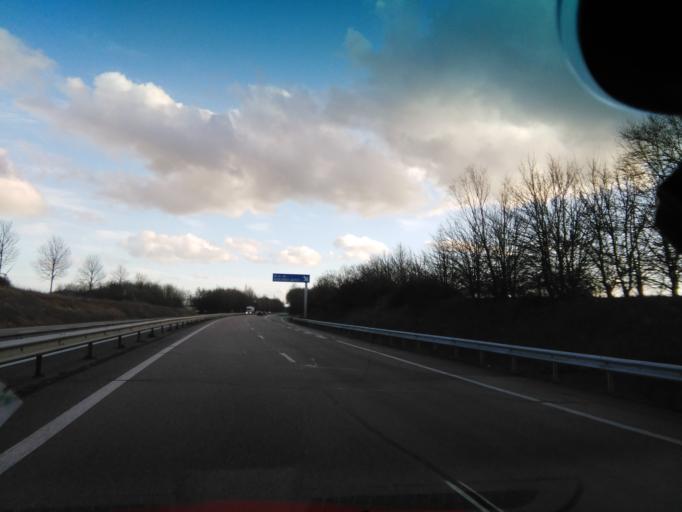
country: FR
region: Lower Normandy
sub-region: Departement du Calvados
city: Potigny
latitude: 48.9404
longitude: -0.2103
